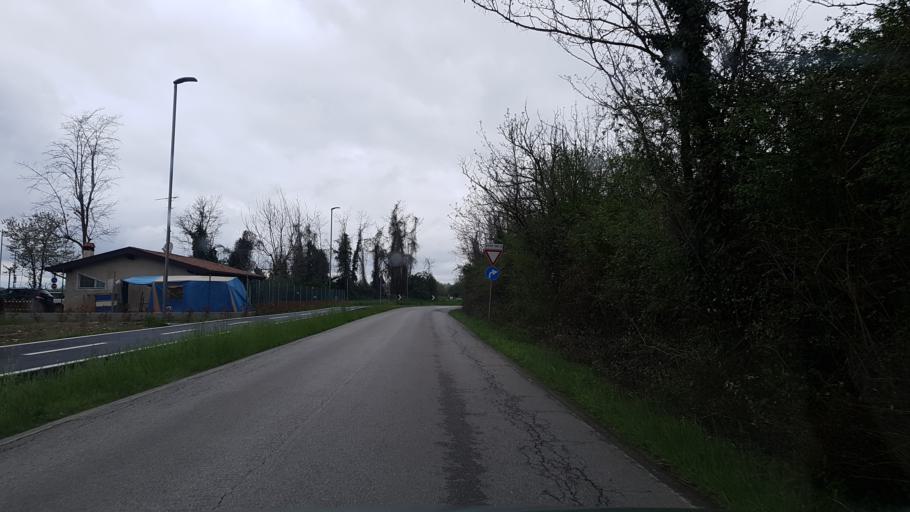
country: IT
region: Friuli Venezia Giulia
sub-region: Provincia di Gorizia
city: Turriaco
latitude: 45.8319
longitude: 13.4427
